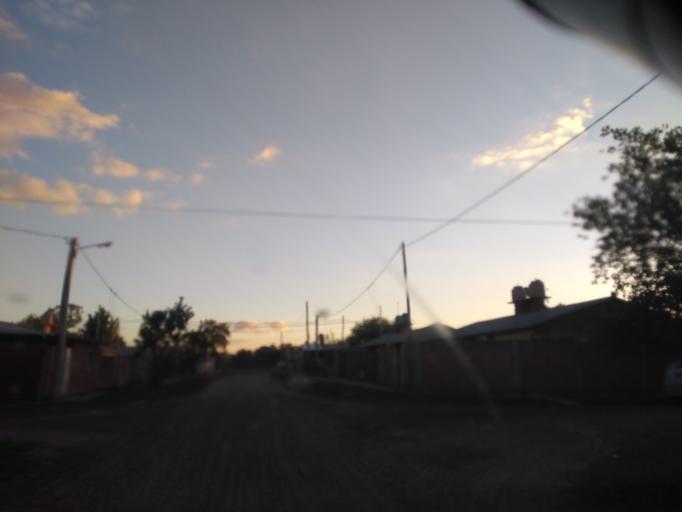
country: AR
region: Chaco
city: Fontana
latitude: -27.4196
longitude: -59.0516
